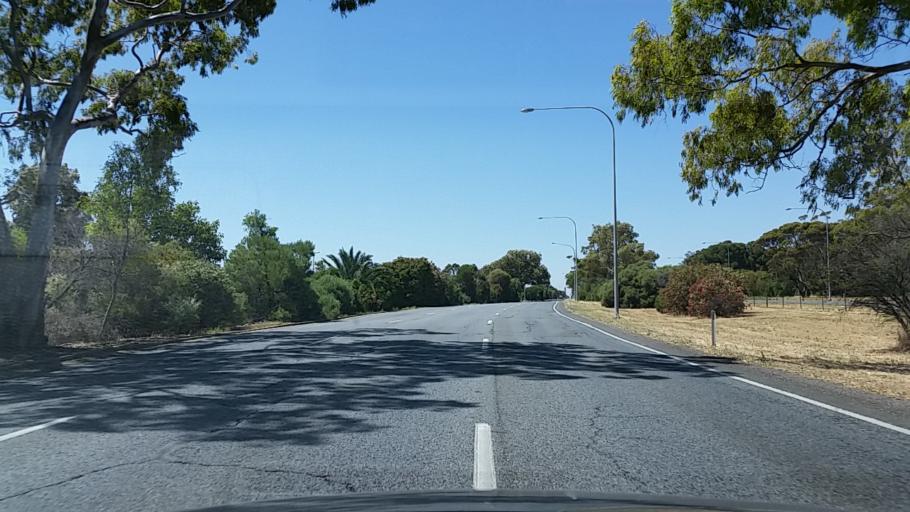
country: AU
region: South Australia
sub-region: Salisbury
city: Elizabeth
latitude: -34.7053
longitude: 138.6796
